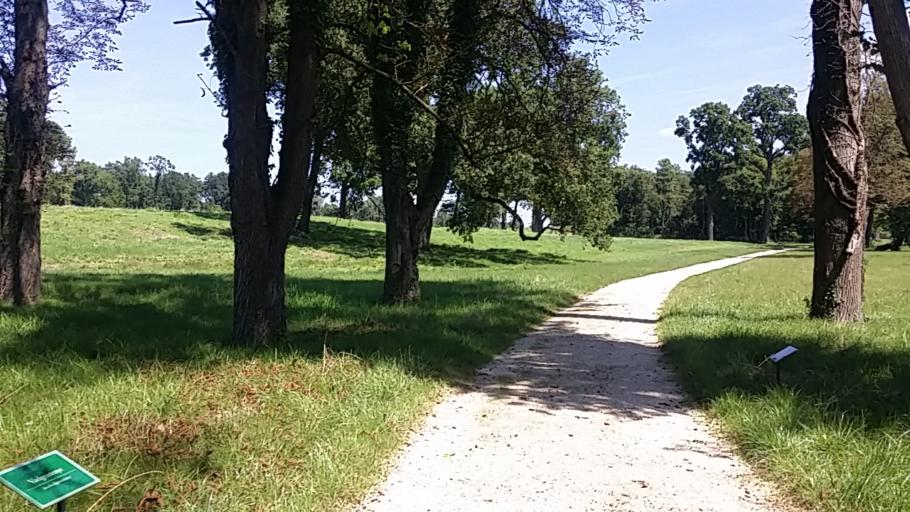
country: HU
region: Fejer
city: Deg
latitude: 46.8642
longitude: 18.4278
